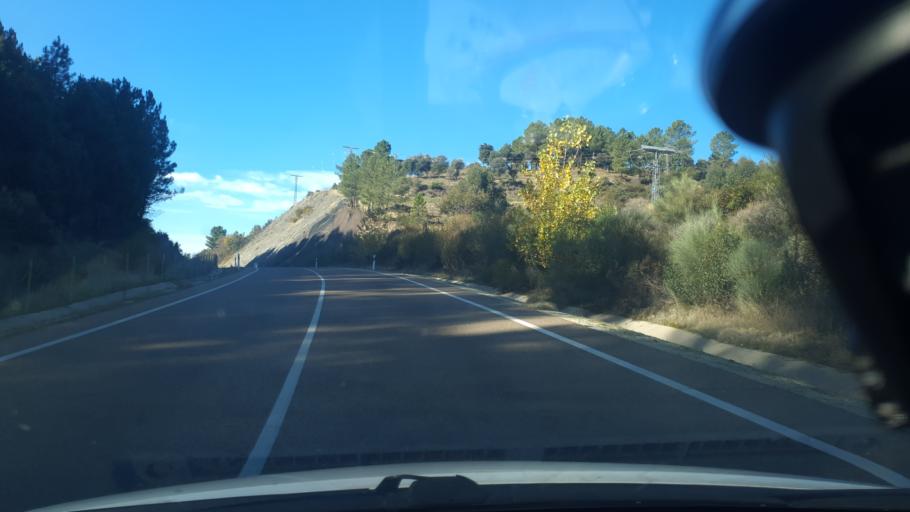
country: ES
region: Castille and Leon
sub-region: Provincia de Avila
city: Poyales del Hoyo
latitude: 40.1684
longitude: -5.1248
